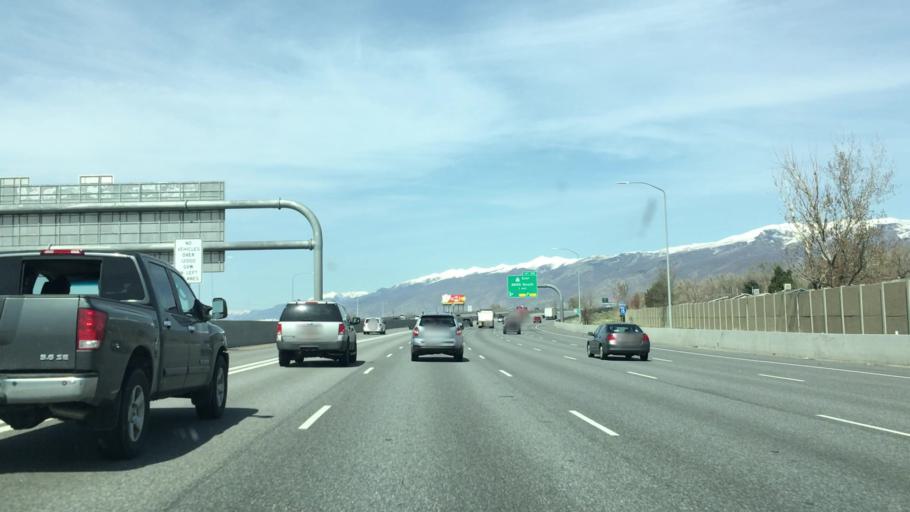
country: US
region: Utah
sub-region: Davis County
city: North Salt Lake
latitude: 40.8449
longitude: -111.9149
